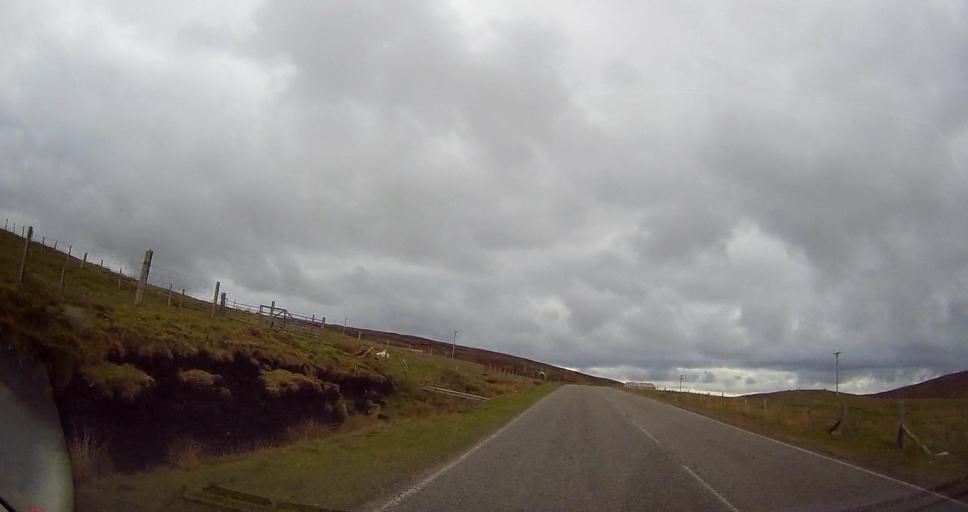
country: GB
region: Scotland
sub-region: Shetland Islands
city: Shetland
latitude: 60.6054
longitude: -1.1085
